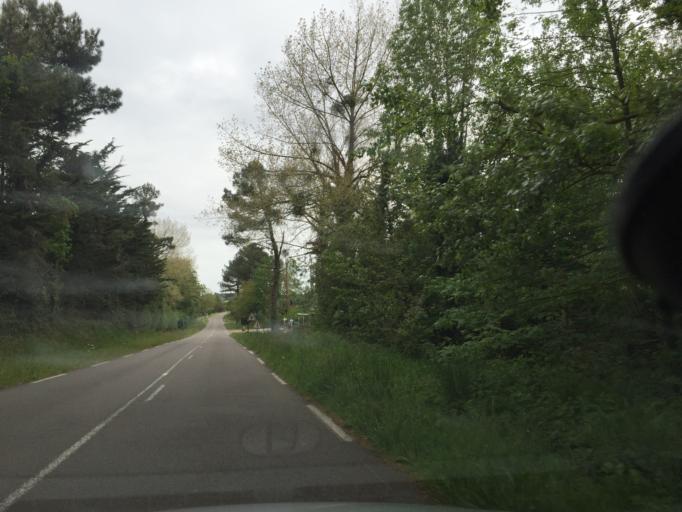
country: FR
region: Brittany
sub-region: Departement des Cotes-d'Armor
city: Plurien
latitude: 48.6533
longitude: -2.3543
